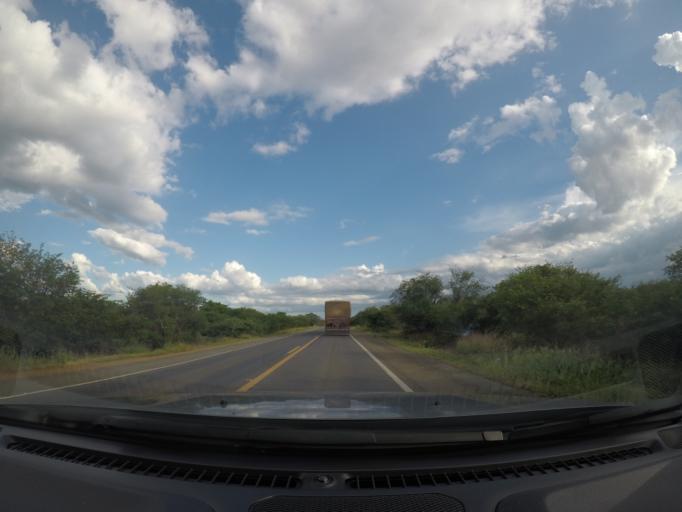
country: BR
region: Bahia
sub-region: Oliveira Dos Brejinhos
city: Beira Rio
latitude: -12.1817
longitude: -42.8332
